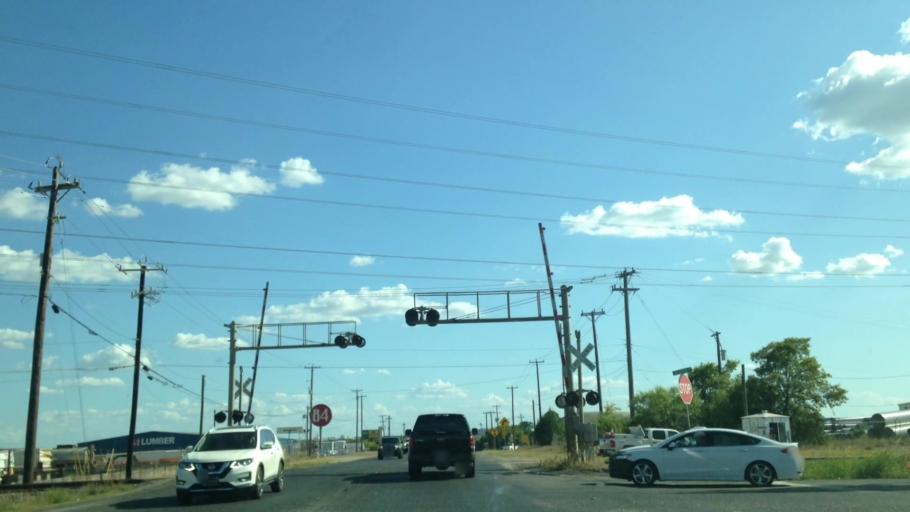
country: US
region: Texas
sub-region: Bexar County
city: Selma
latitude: 29.6092
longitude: -98.3255
